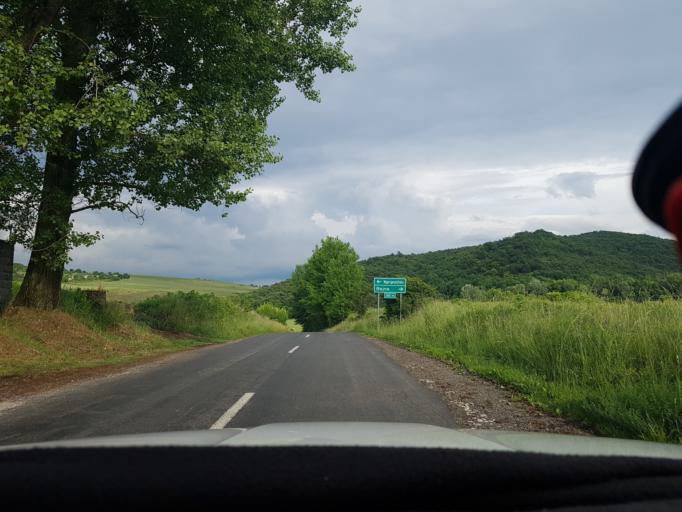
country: HU
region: Komarom-Esztergom
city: Nyergesujfalu
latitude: 47.7168
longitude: 18.5602
